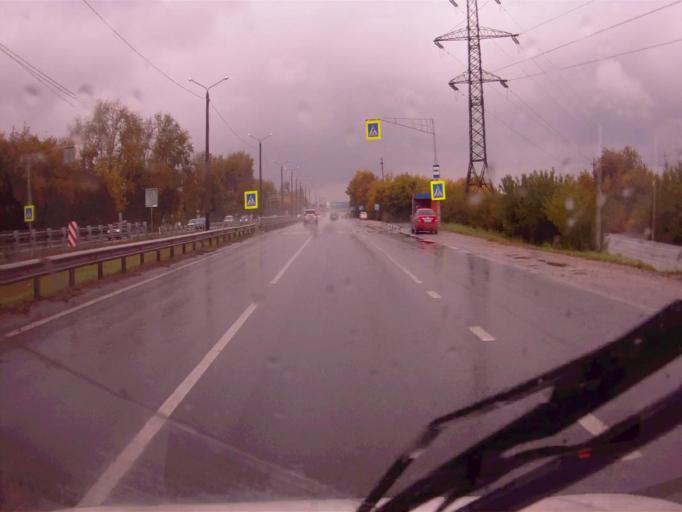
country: RU
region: Chelyabinsk
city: Dolgoderevenskoye
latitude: 55.2571
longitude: 61.3516
